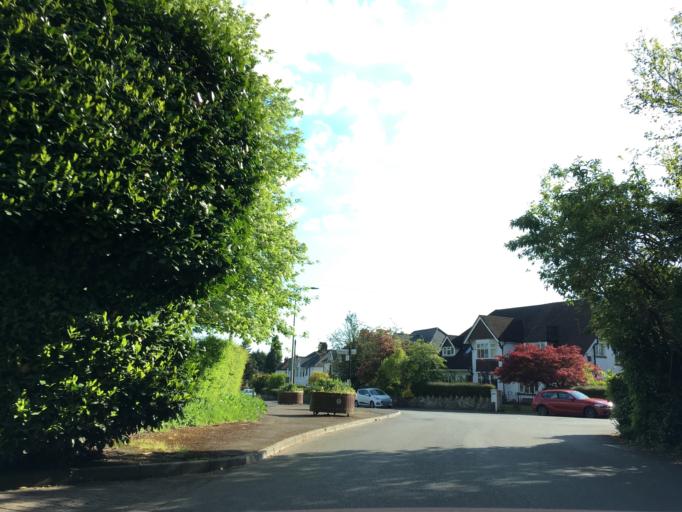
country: GB
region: Wales
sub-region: Newport
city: Marshfield
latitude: 51.5330
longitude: -3.1112
